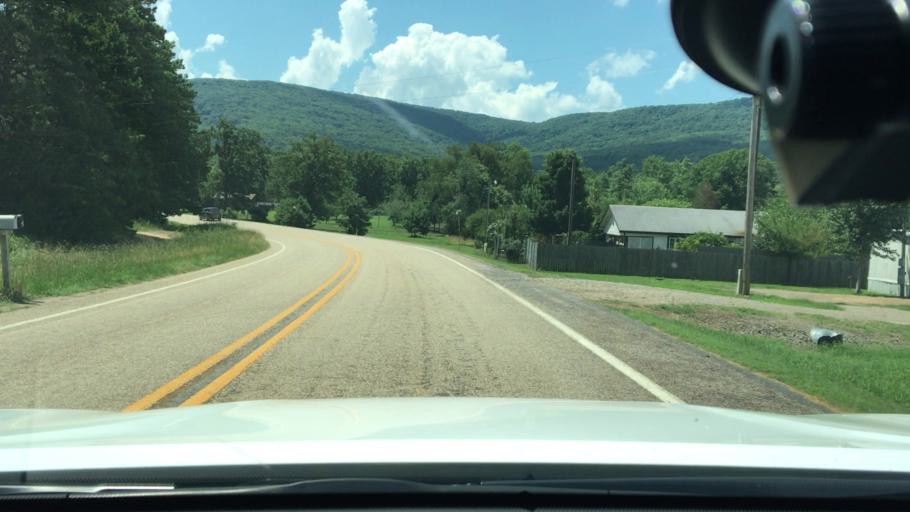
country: US
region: Arkansas
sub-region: Logan County
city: Paris
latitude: 35.1981
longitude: -93.6349
